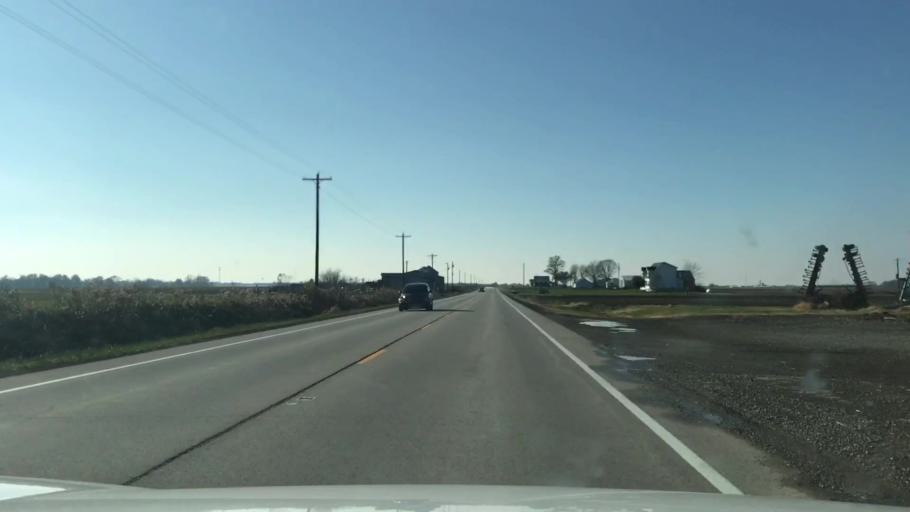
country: US
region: Illinois
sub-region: Washington County
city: Okawville
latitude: 38.4424
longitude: -89.5028
